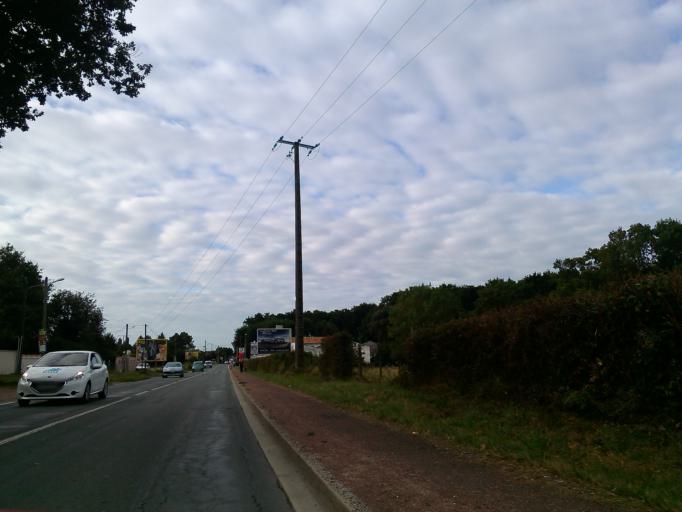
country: FR
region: Poitou-Charentes
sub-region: Departement de la Charente-Maritime
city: Royan
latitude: 45.6482
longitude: -1.0244
